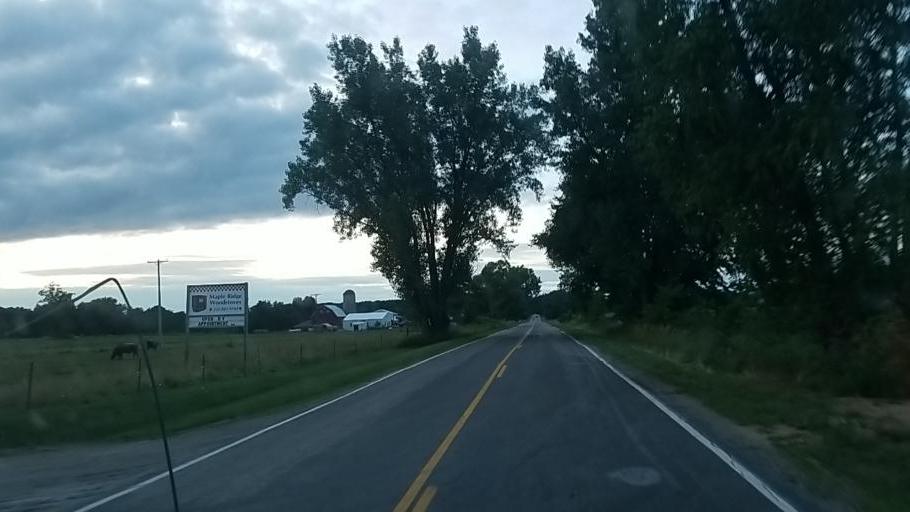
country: US
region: Michigan
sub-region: Newaygo County
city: Fremont
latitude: 43.4750
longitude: -86.0792
